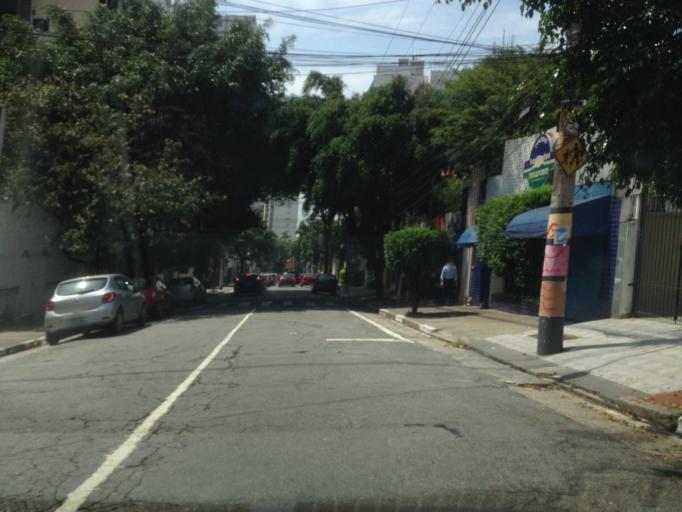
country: BR
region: Sao Paulo
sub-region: Sao Paulo
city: Sao Paulo
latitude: -23.5600
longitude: -46.6752
